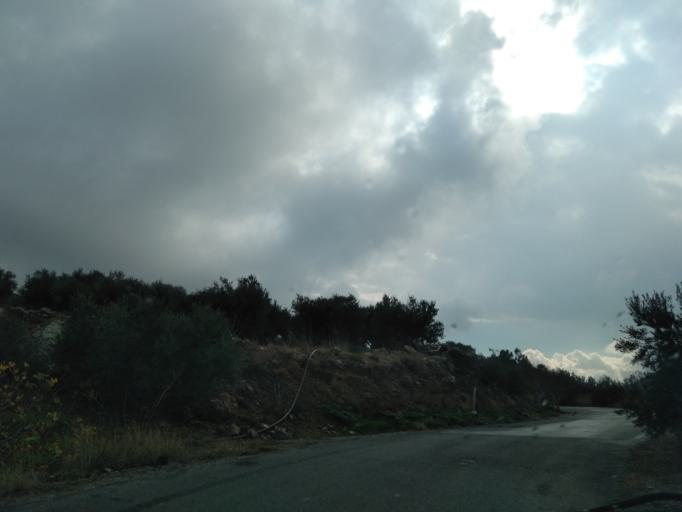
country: GR
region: Crete
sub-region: Nomos Lasithiou
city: Siteia
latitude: 35.1494
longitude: 26.0208
